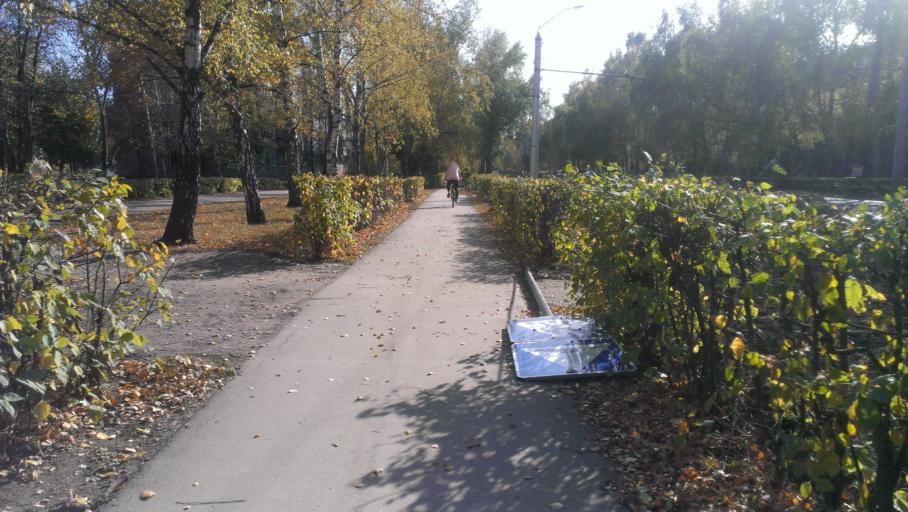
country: RU
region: Altai Krai
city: Novosilikatnyy
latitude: 53.3529
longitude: 83.6842
